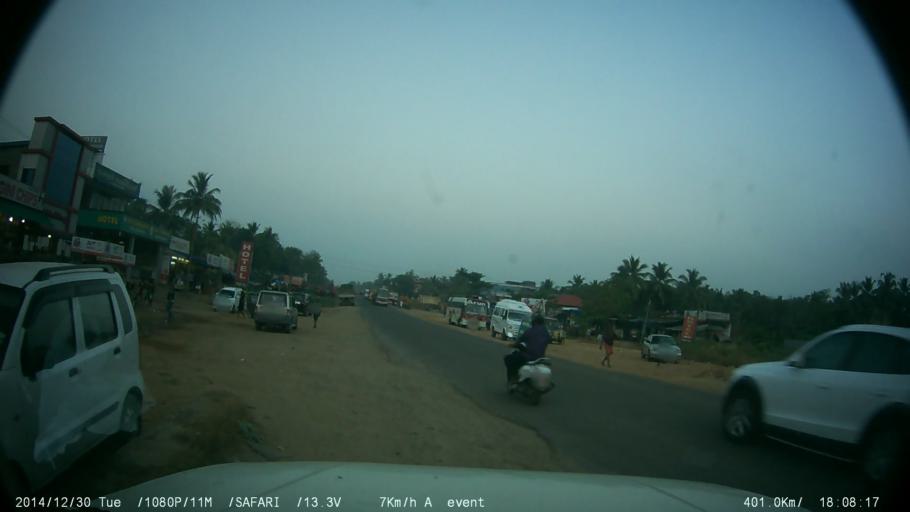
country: IN
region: Kerala
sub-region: Thrissur District
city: Chelakara
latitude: 10.6016
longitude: 76.4914
